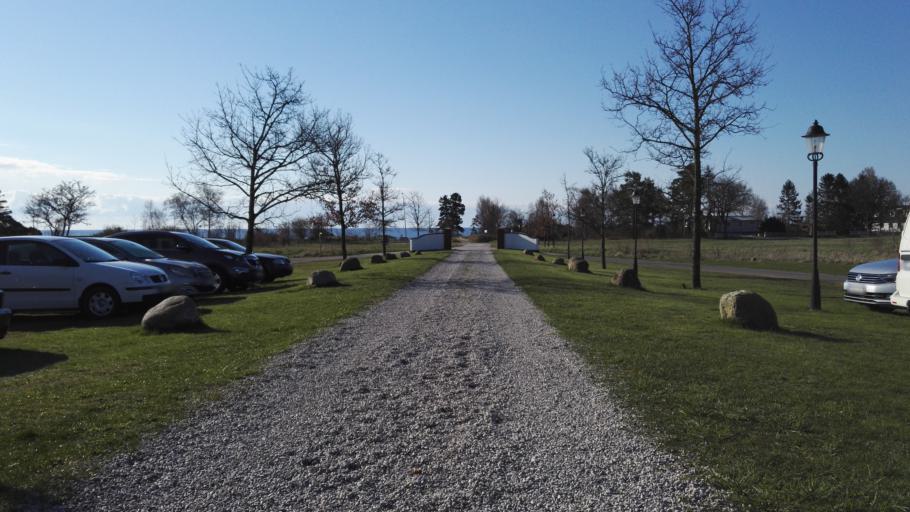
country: SE
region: Skane
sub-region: Skurups Kommun
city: Skivarp
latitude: 55.4147
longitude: 13.6241
